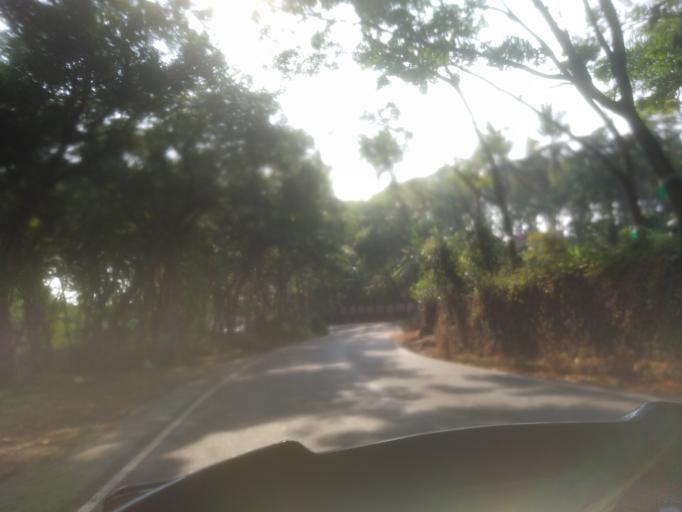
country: IN
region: Kerala
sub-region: Ernakulam
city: Piravam
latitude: 9.8659
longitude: 76.5368
